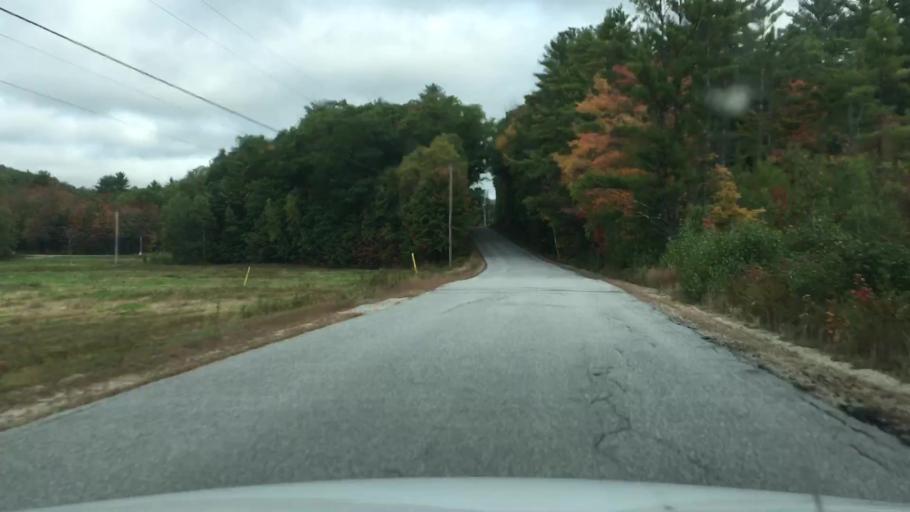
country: US
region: Maine
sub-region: Cumberland County
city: Harrison
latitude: 44.2522
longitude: -70.7228
